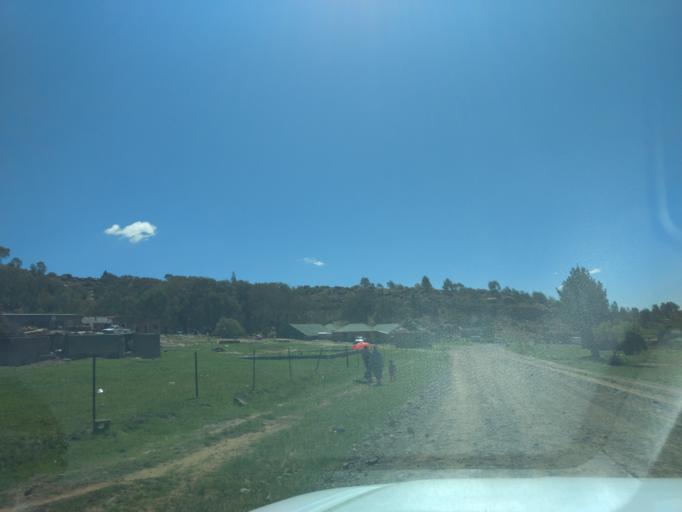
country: LS
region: Maseru
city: Maseru
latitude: -29.4942
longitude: 27.3730
